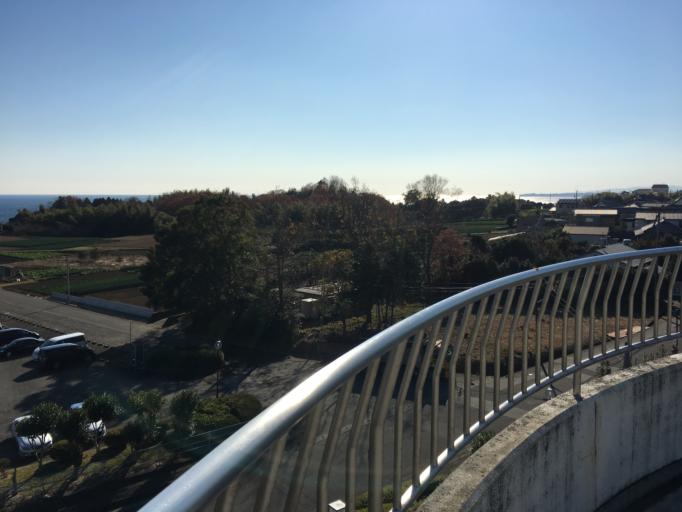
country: JP
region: Fukushima
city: Iwaki
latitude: 36.9255
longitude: 140.8560
